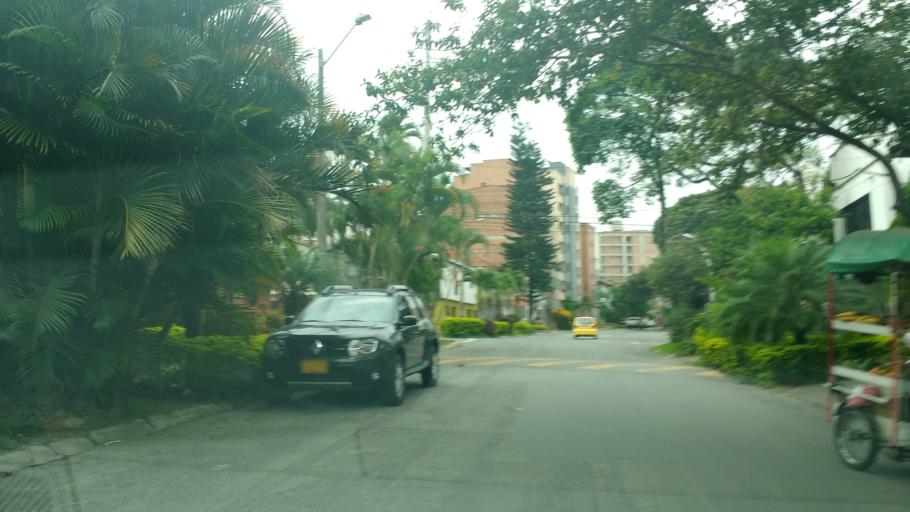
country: CO
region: Antioquia
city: Medellin
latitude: 6.2526
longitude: -75.5928
